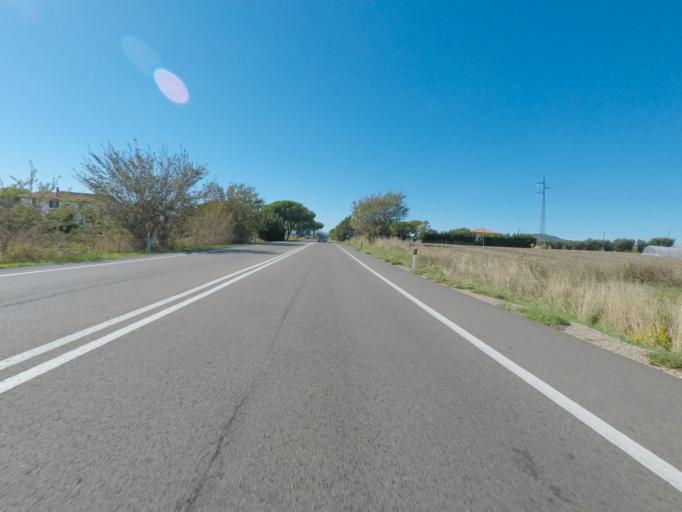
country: IT
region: Tuscany
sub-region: Provincia di Grosseto
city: Capalbio
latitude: 42.4148
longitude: 11.4043
